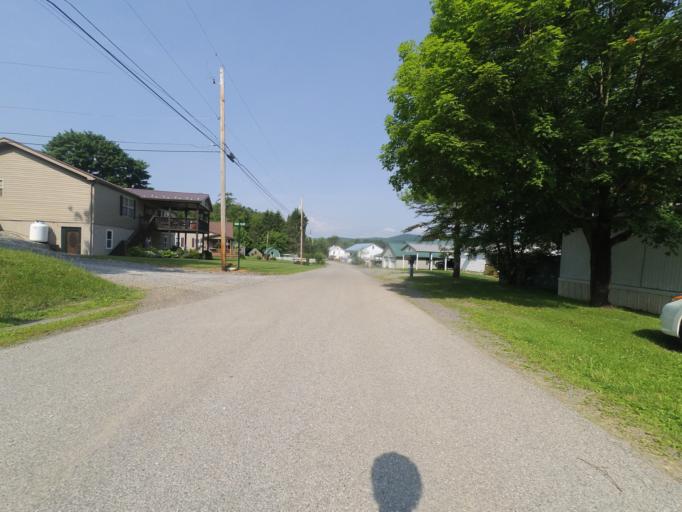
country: US
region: Pennsylvania
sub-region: Centre County
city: Zion
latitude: 40.9720
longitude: -77.7222
